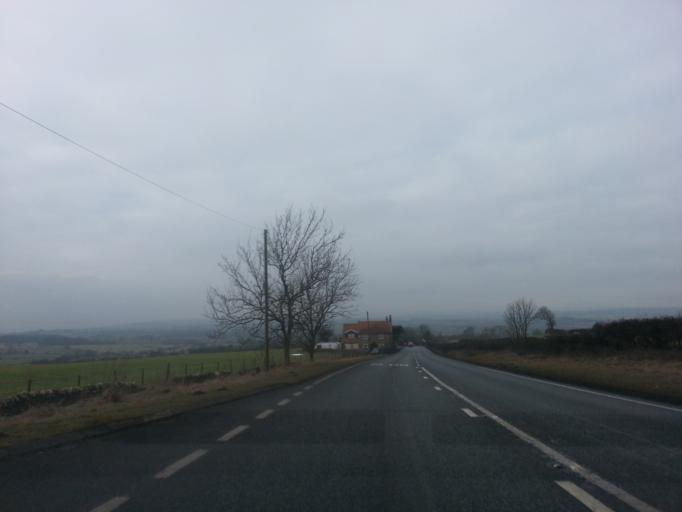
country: GB
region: England
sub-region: County Durham
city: Bishop Auckland
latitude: 54.6134
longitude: -1.6917
